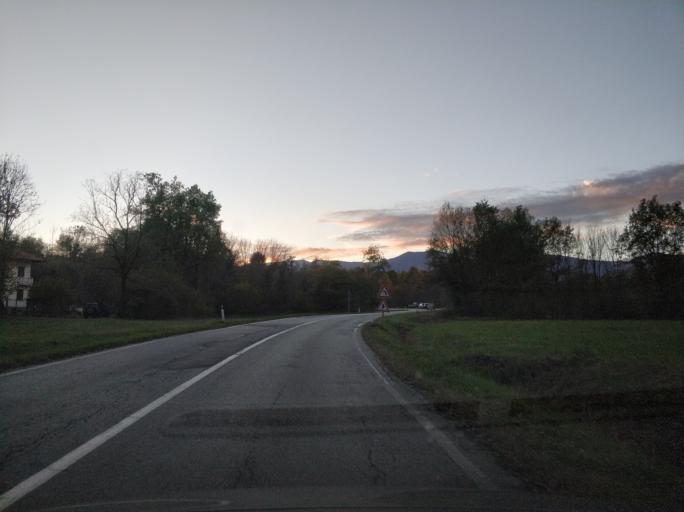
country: IT
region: Piedmont
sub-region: Provincia di Torino
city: Robassomero
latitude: 45.2031
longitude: 7.5700
